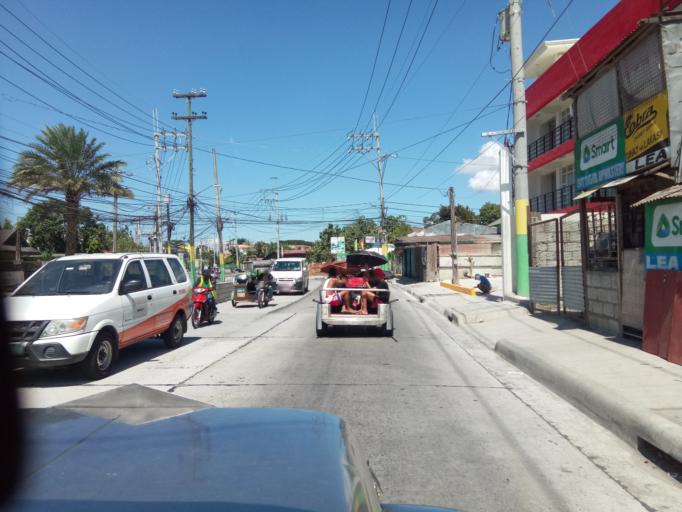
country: PH
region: Calabarzon
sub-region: Province of Cavite
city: Dasmarinas
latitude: 14.3505
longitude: 120.9418
